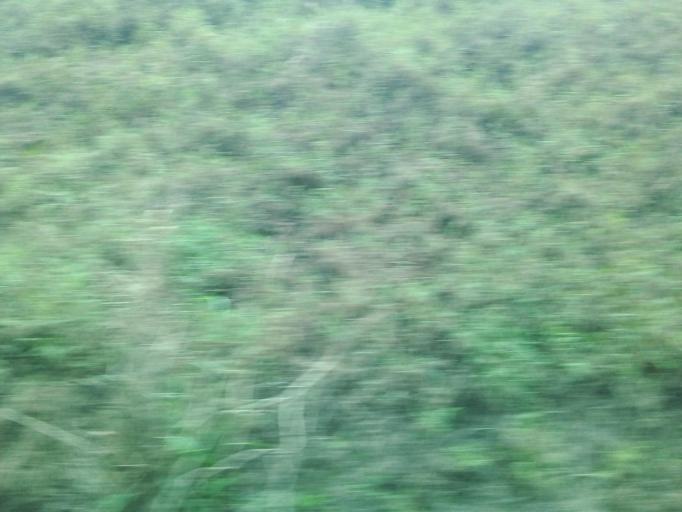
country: BR
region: Minas Gerais
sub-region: Timoteo
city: Timoteo
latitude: -19.5636
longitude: -42.7153
